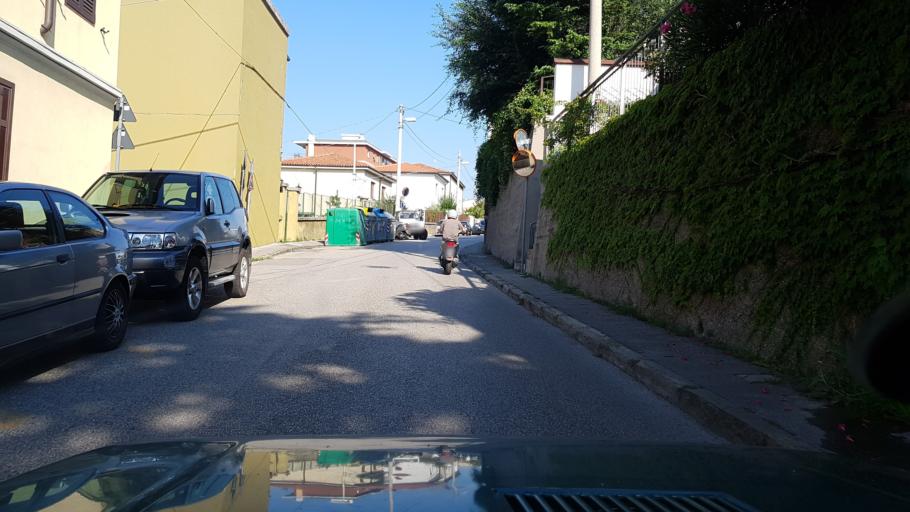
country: IT
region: Friuli Venezia Giulia
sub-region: Provincia di Trieste
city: Trieste
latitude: 45.6353
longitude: 13.7891
